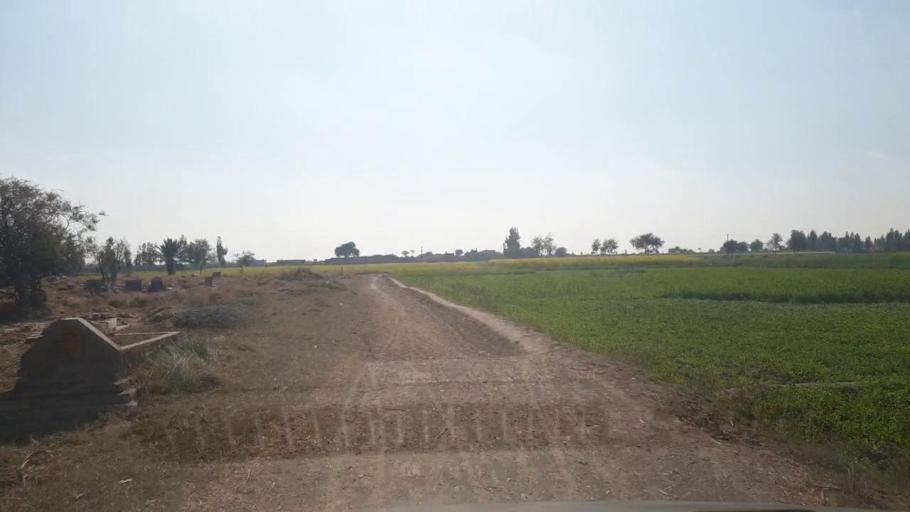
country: PK
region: Sindh
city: Shahdadpur
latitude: 25.9262
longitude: 68.5810
